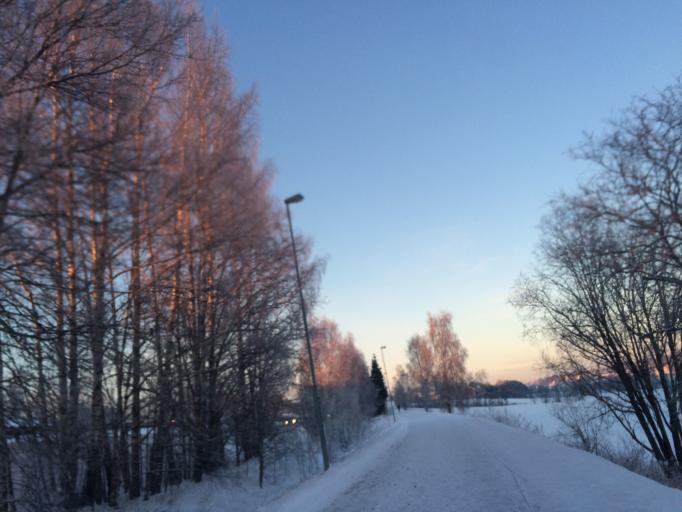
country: NO
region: Akershus
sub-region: Ski
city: Ski
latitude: 59.6974
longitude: 10.8327
